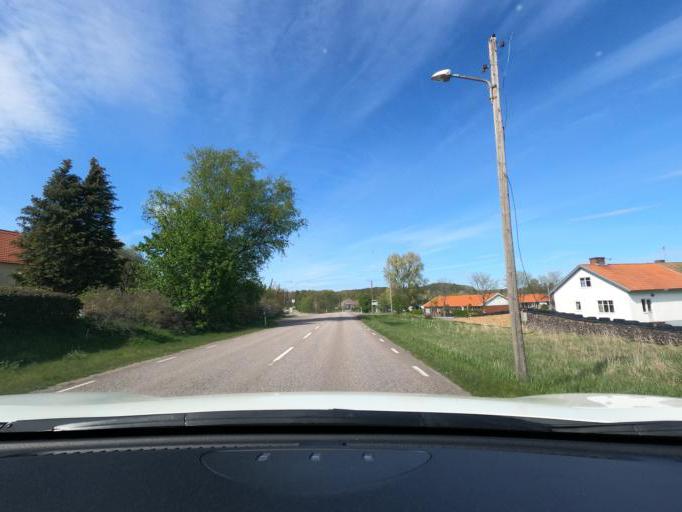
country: SE
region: Vaestra Goetaland
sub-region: Marks Kommun
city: Kinna
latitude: 57.4670
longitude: 12.5935
